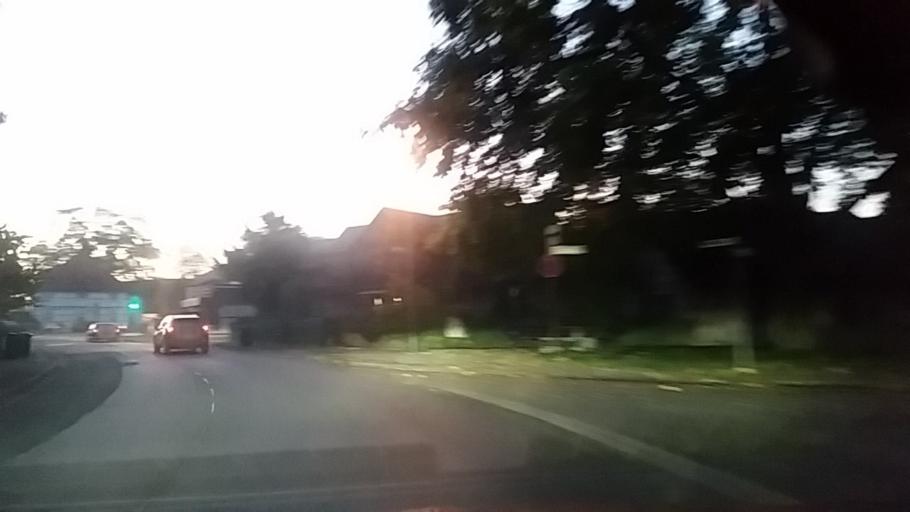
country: DE
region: Lower Saxony
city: Wolfsburg
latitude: 52.3934
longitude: 10.7315
